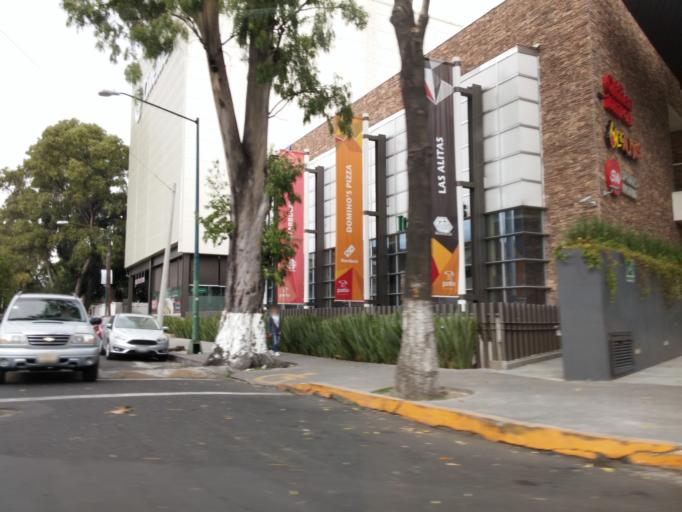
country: MX
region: Mexico City
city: Azcapotzalco
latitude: 19.4636
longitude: -99.1823
